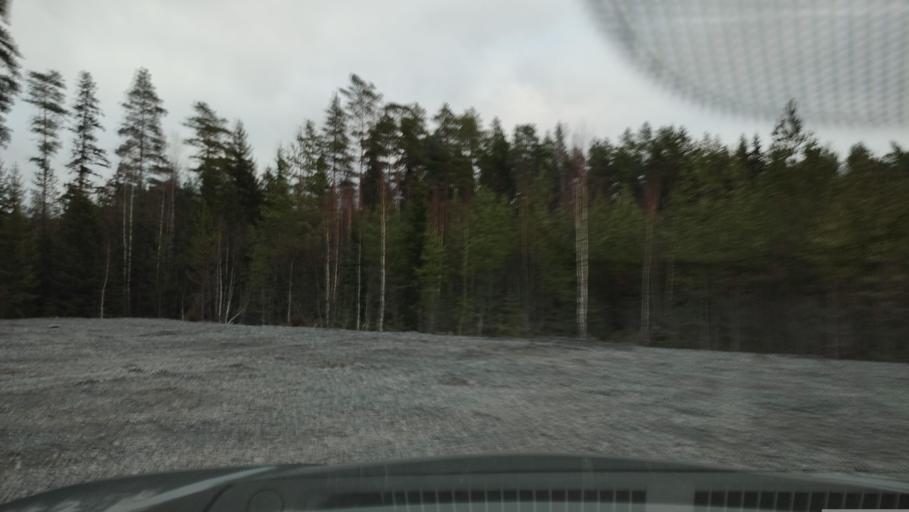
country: FI
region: Southern Ostrobothnia
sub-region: Suupohja
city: Karijoki
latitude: 62.1951
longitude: 21.5976
